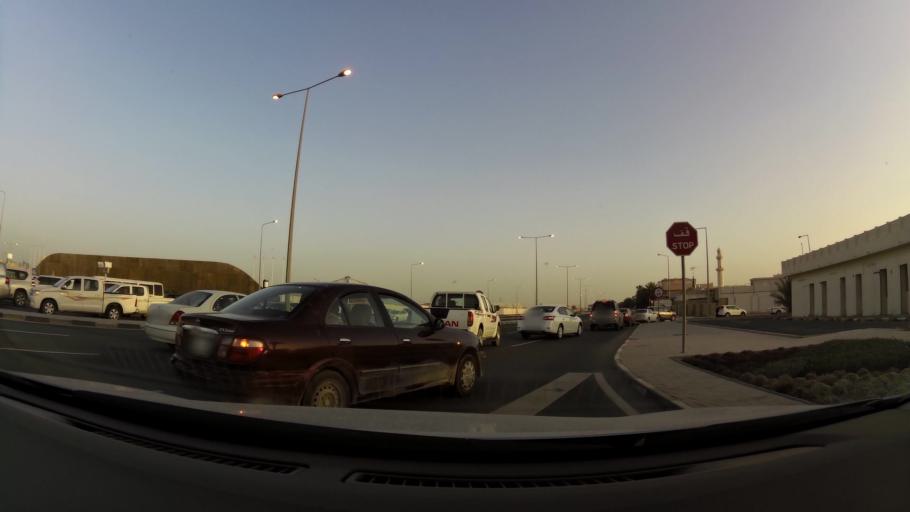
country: QA
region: Baladiyat ad Dawhah
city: Doha
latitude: 25.3217
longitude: 51.4862
